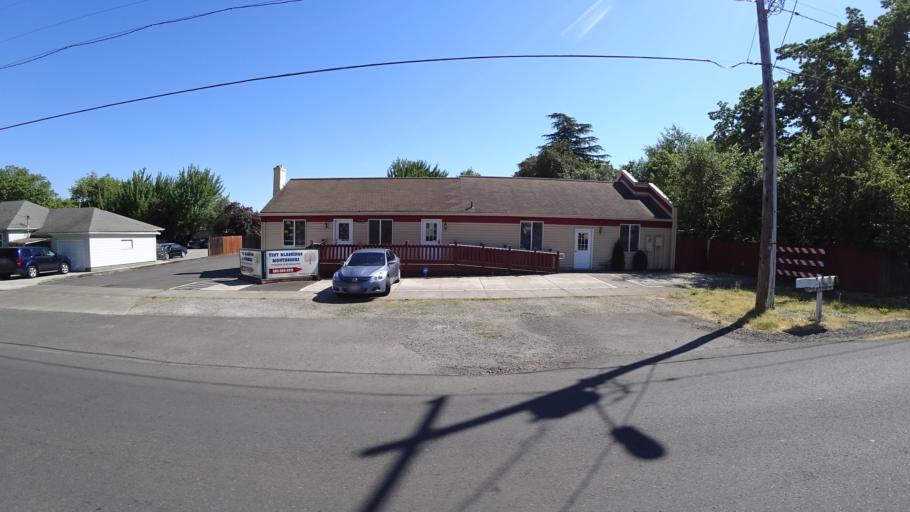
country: US
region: Oregon
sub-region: Washington County
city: Aloha
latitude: 45.4959
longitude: -122.8742
